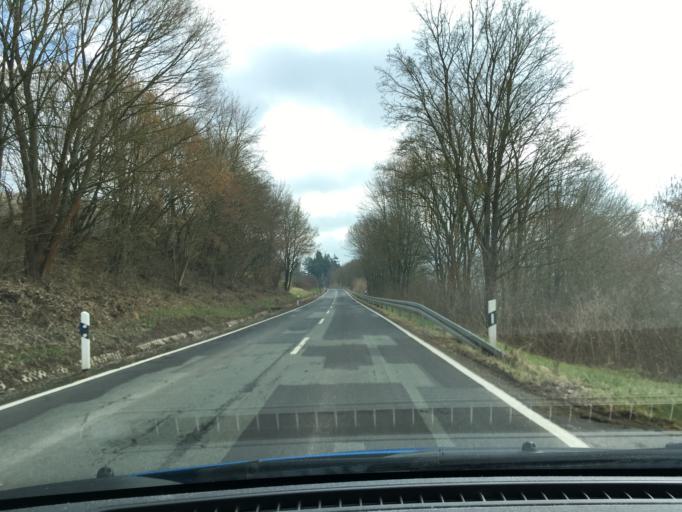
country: DE
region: Lower Saxony
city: Bodenfelde
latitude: 51.5713
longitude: 9.5982
